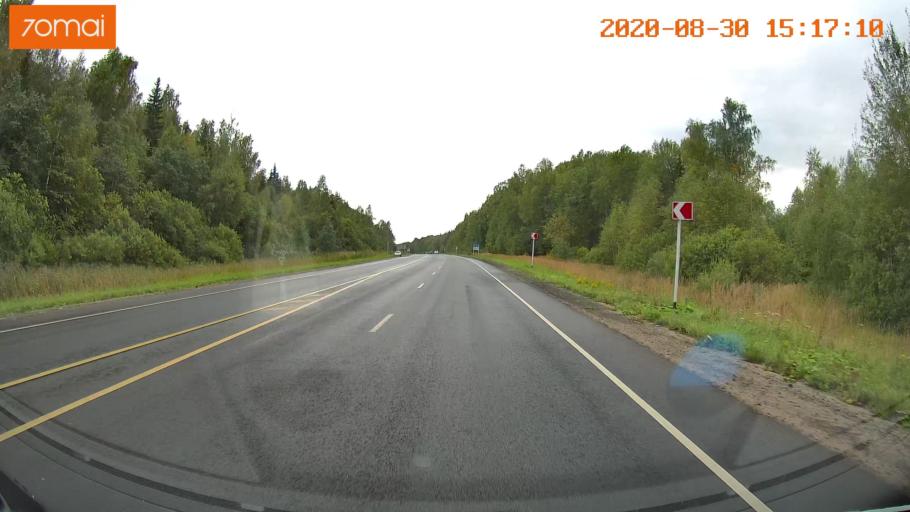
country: RU
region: Ivanovo
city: Rodniki
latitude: 57.1374
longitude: 41.8085
